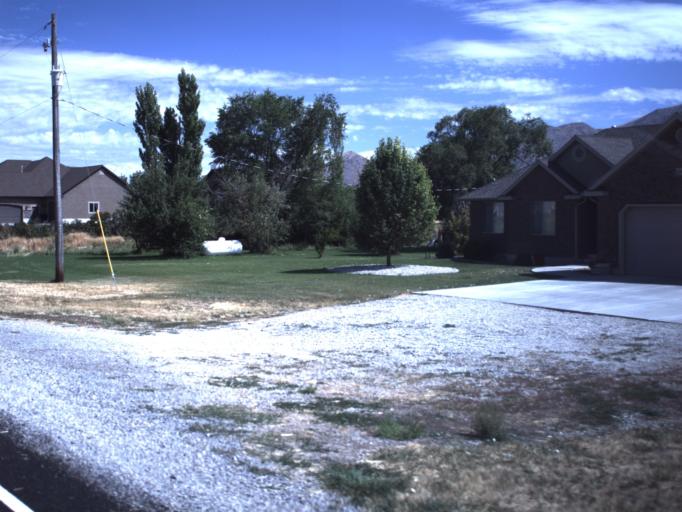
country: US
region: Utah
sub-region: Box Elder County
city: Elwood
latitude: 41.6616
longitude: -112.1406
